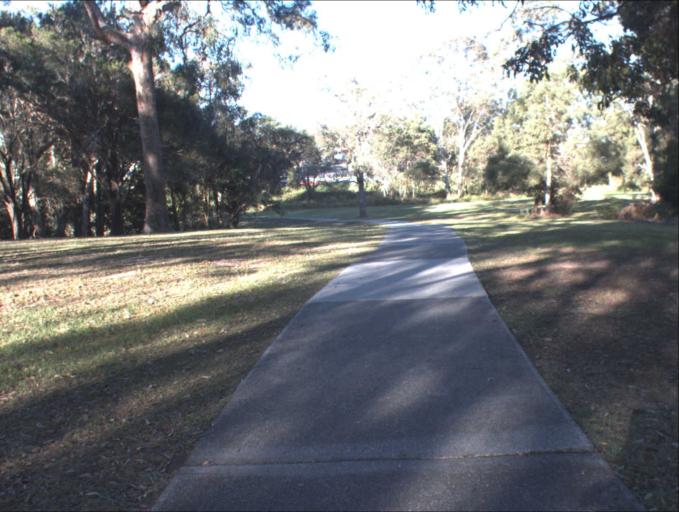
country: AU
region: Queensland
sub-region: Logan
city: Logan City
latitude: -27.6350
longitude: 153.1282
